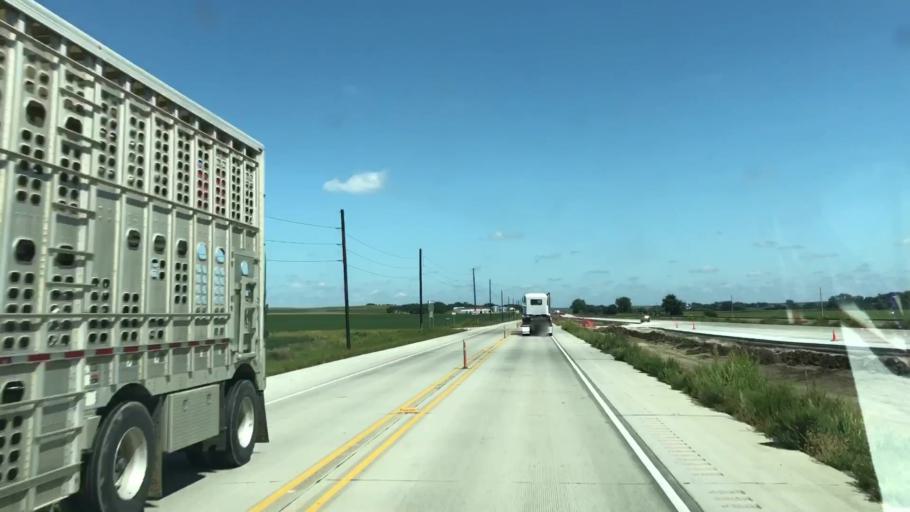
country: US
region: Iowa
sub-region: Plymouth County
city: Le Mars
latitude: 42.7286
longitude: -96.2344
